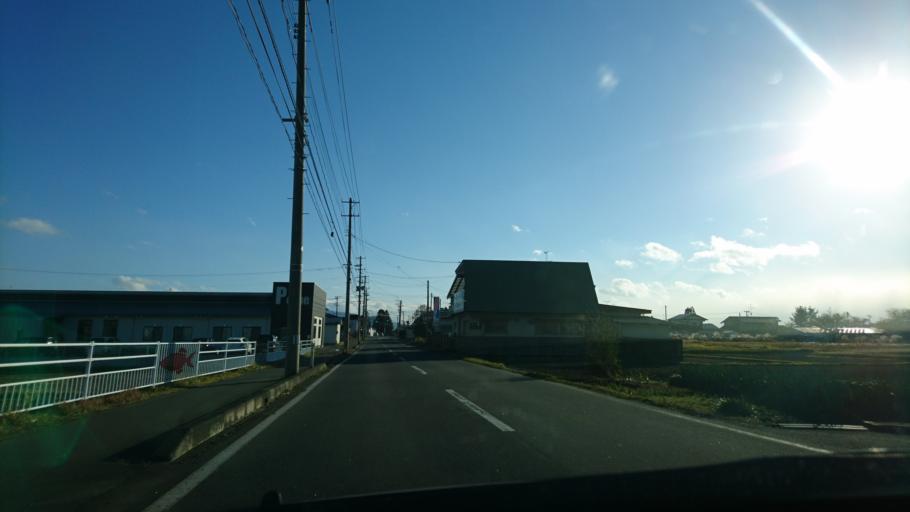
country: JP
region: Iwate
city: Mizusawa
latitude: 39.1211
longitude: 141.1557
